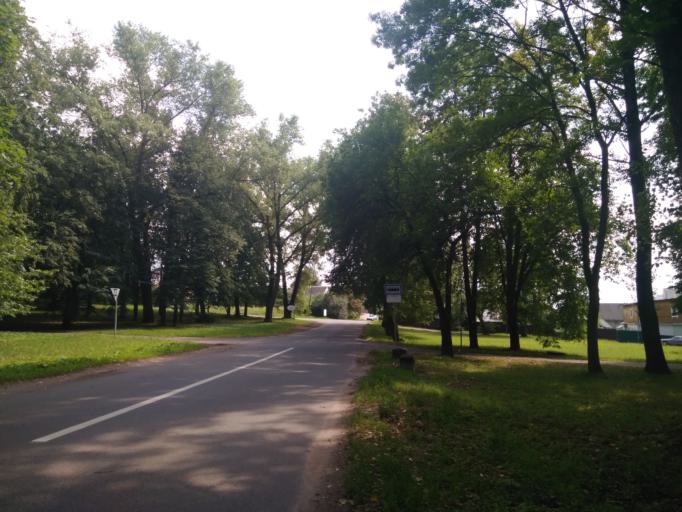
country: BY
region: Minsk
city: Minsk
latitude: 53.9399
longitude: 27.5557
